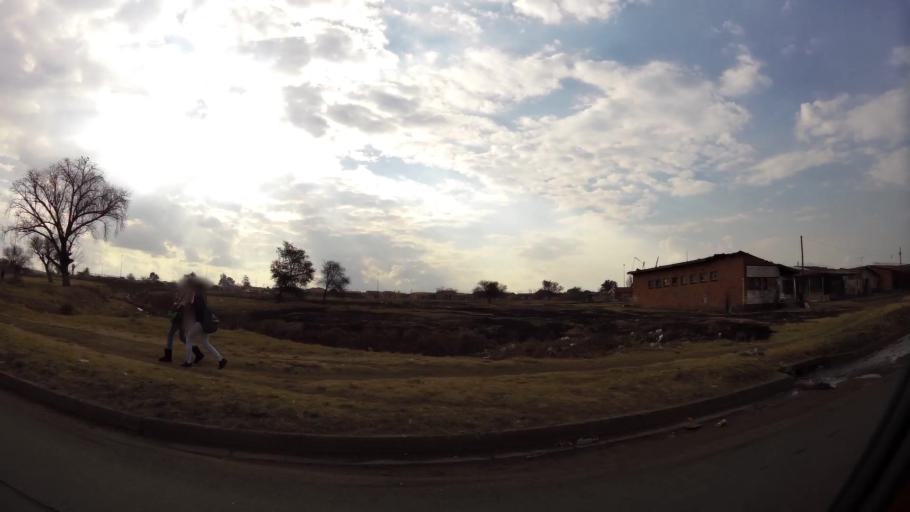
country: ZA
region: Gauteng
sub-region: Sedibeng District Municipality
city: Vereeniging
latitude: -26.6787
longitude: 27.8874
